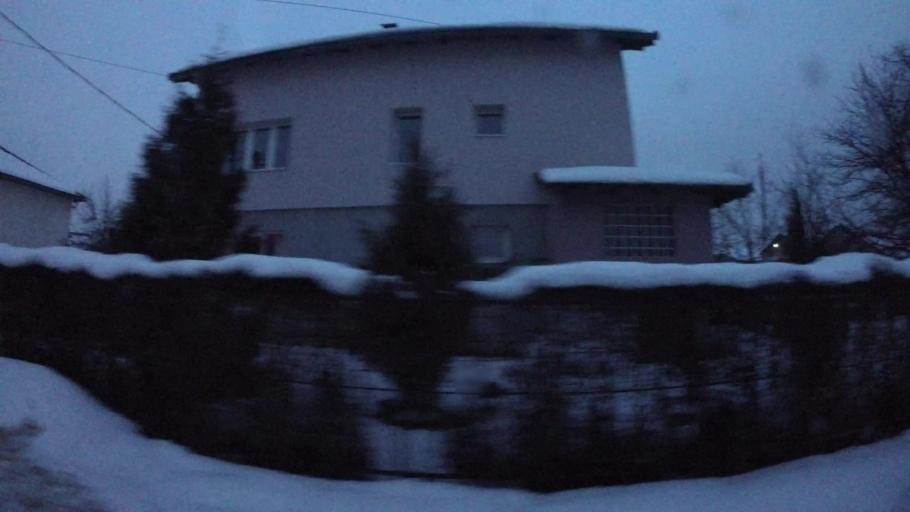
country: BA
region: Federation of Bosnia and Herzegovina
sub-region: Kanton Sarajevo
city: Sarajevo
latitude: 43.8399
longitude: 18.2943
